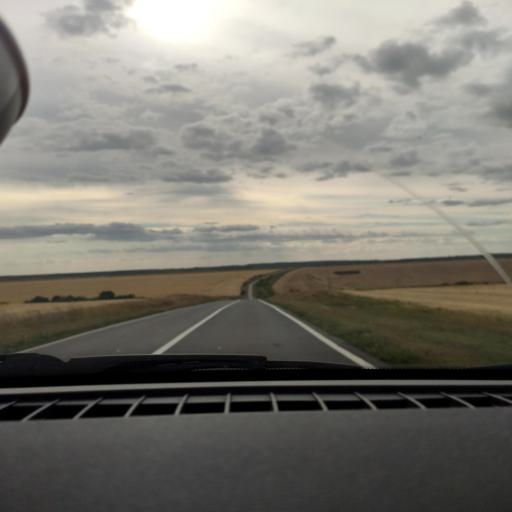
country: RU
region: Samara
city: Georgiyevka
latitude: 53.4167
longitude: 50.8897
